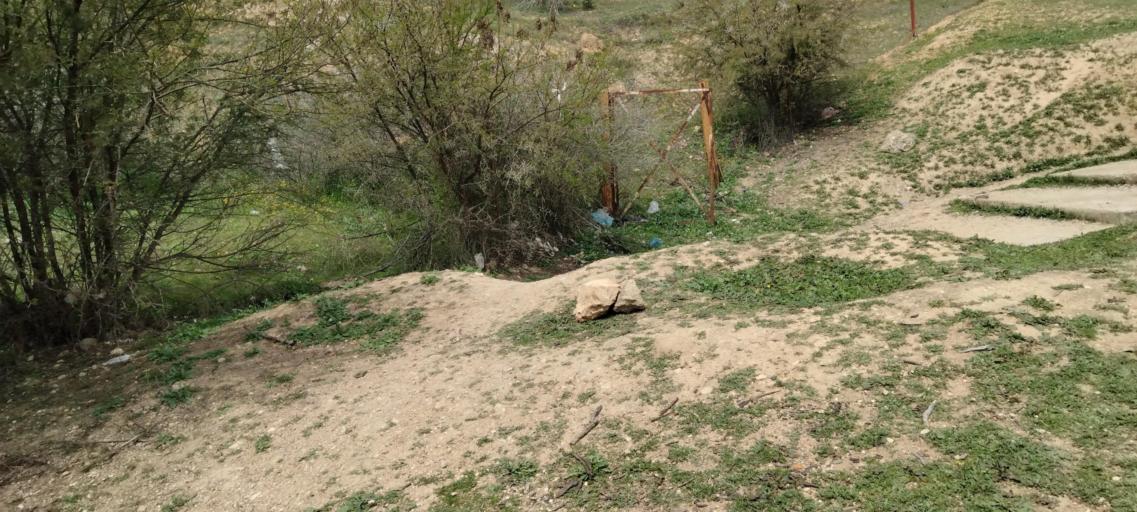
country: MA
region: Fes-Boulemane
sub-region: Fes
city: Fes
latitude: 34.0686
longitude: -4.9817
